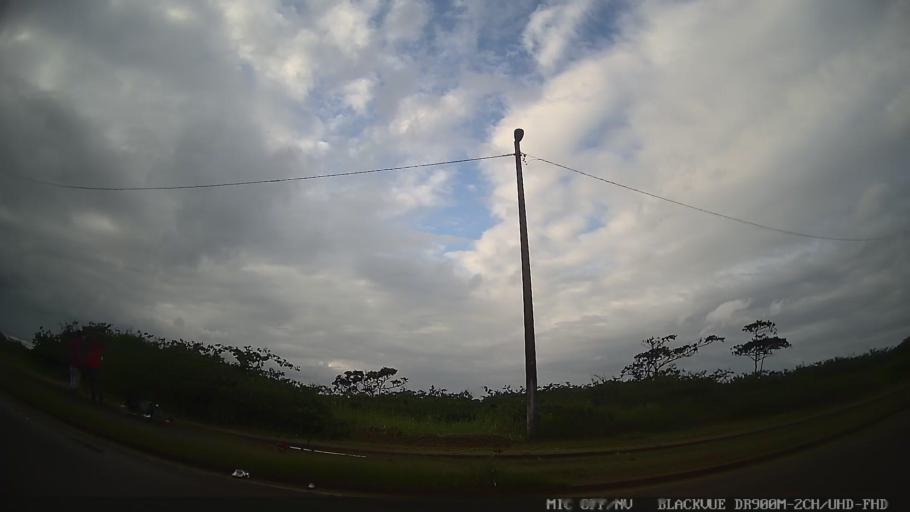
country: BR
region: Sao Paulo
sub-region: Itanhaem
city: Itanhaem
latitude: -24.2406
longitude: -46.8820
